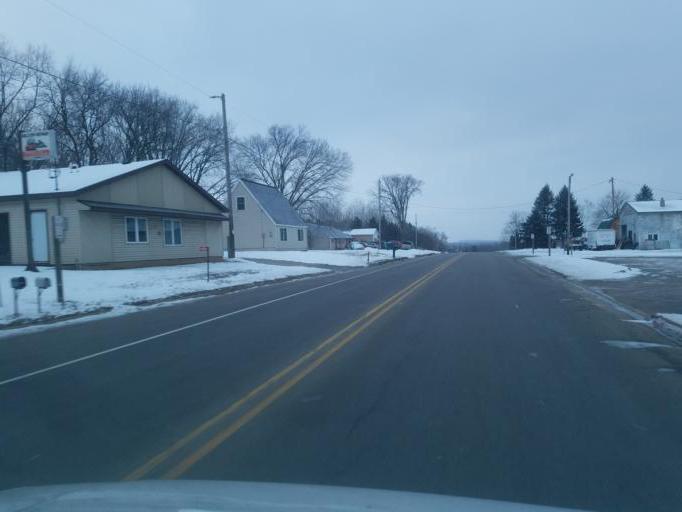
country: US
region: Wisconsin
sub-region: Waupaca County
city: New London
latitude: 44.4098
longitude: -88.7947
